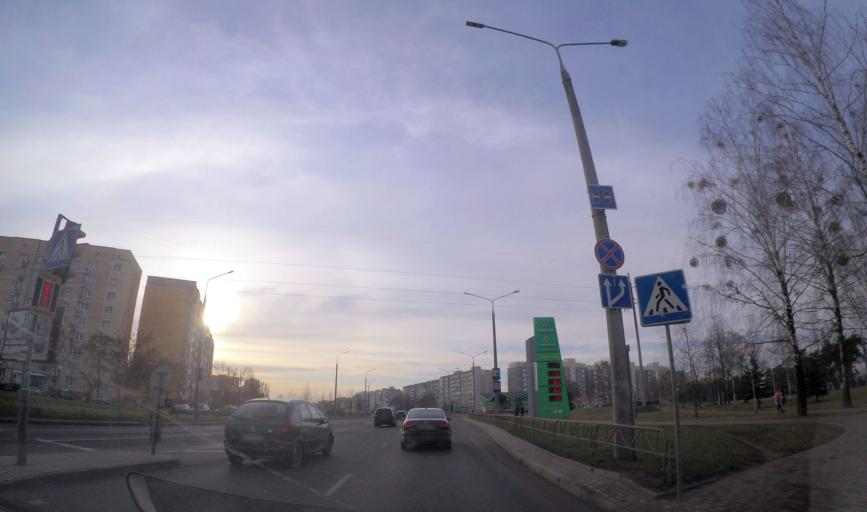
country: BY
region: Grodnenskaya
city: Hrodna
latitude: 53.6658
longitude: 23.7861
